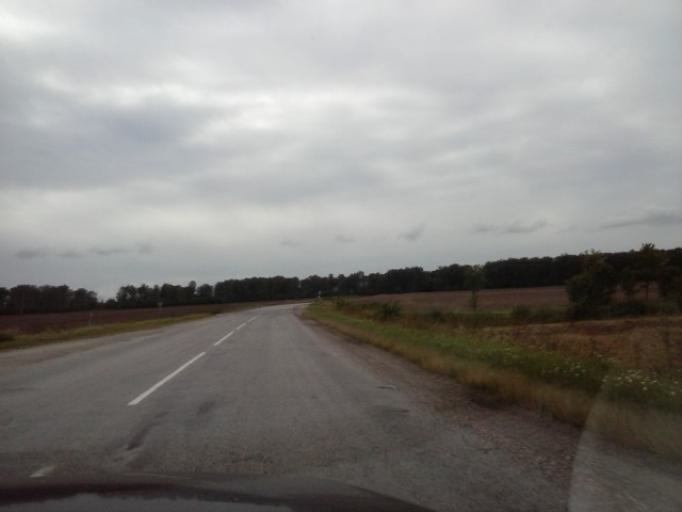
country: LV
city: Tervete
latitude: 56.4511
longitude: 23.4200
